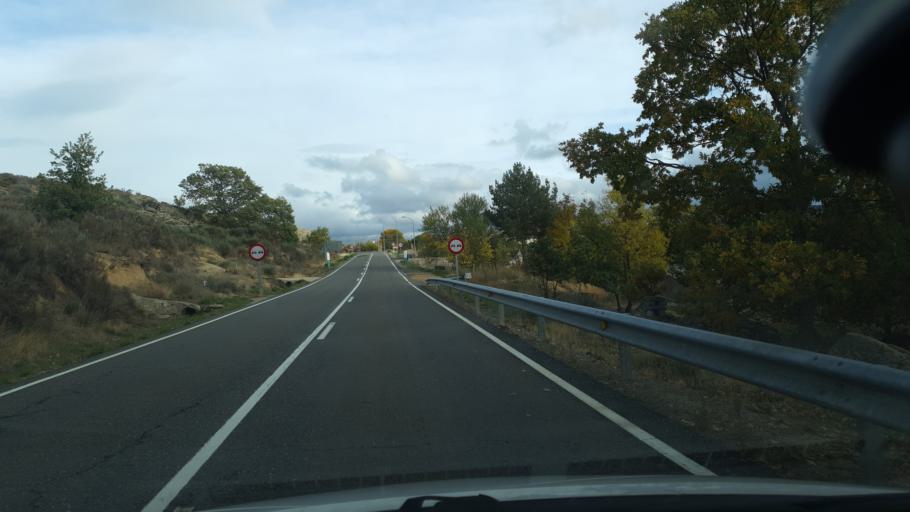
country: ES
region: Castille and Leon
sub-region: Provincia de Avila
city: Navalosa
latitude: 40.3991
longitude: -4.9386
